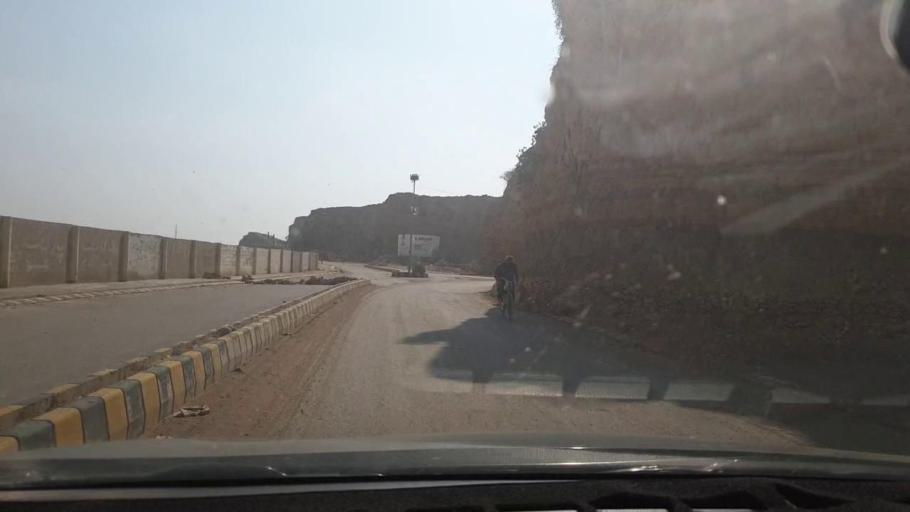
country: PK
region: Sindh
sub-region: Karachi District
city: Karachi
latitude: 24.9688
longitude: 66.9979
